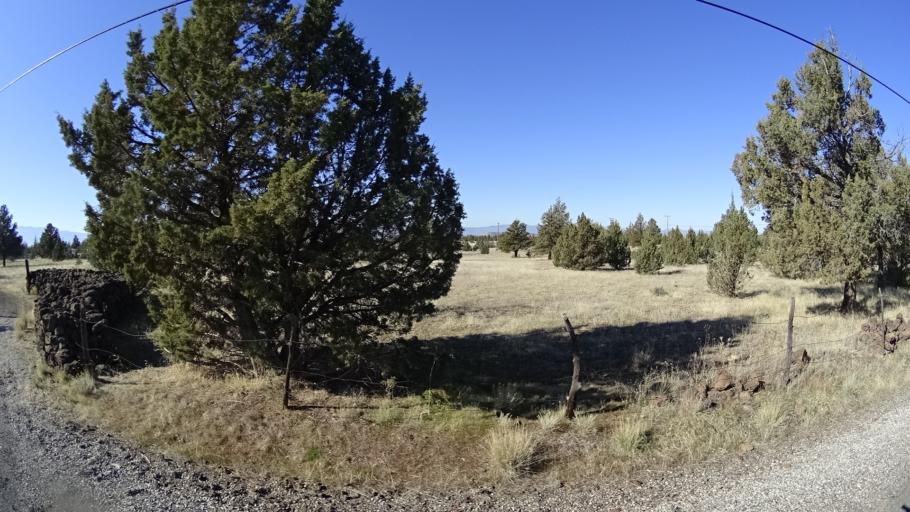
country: US
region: California
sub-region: Siskiyou County
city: Montague
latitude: 41.6486
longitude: -122.3599
